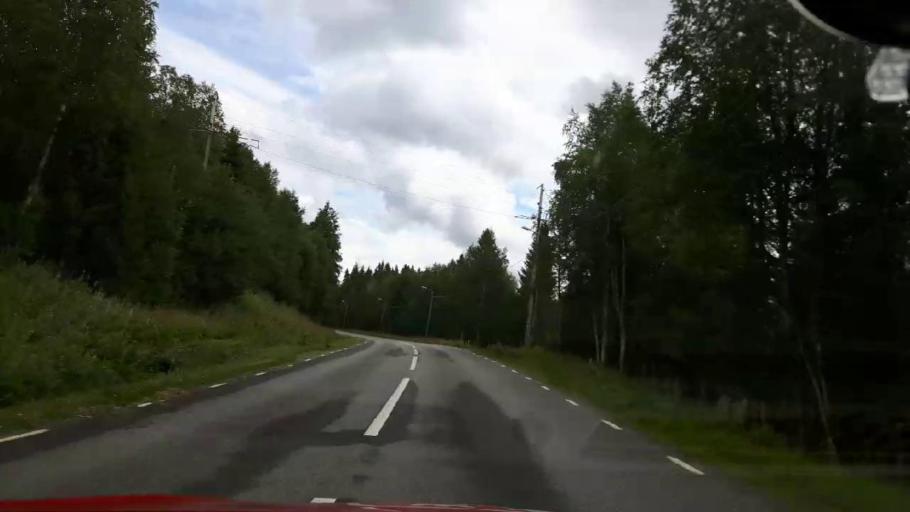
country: NO
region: Nord-Trondelag
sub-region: Lierne
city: Sandvika
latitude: 64.3904
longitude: 14.3780
